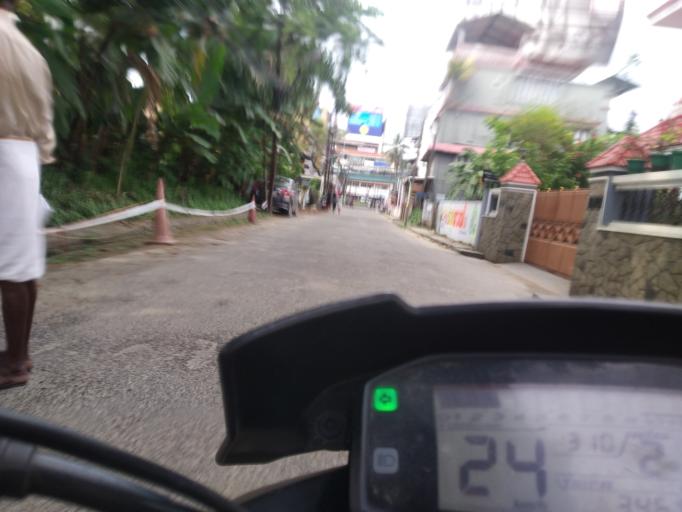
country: IN
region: Kerala
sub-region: Ernakulam
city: Cochin
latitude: 9.9638
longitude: 76.2918
